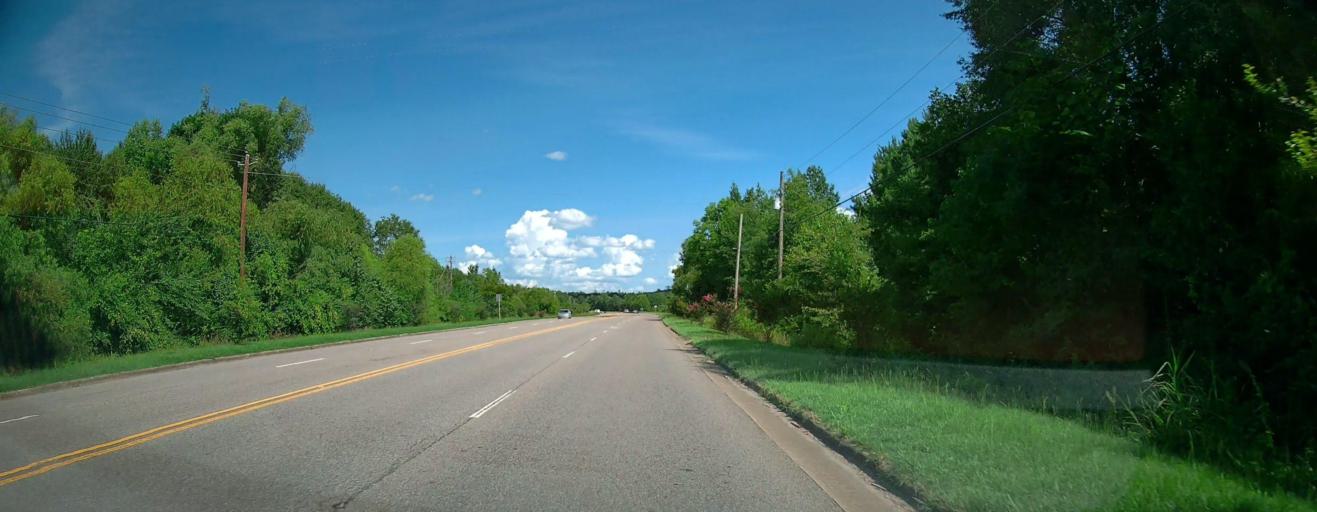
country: US
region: Alabama
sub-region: Pickens County
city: Reform
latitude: 33.3761
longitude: -88.0083
